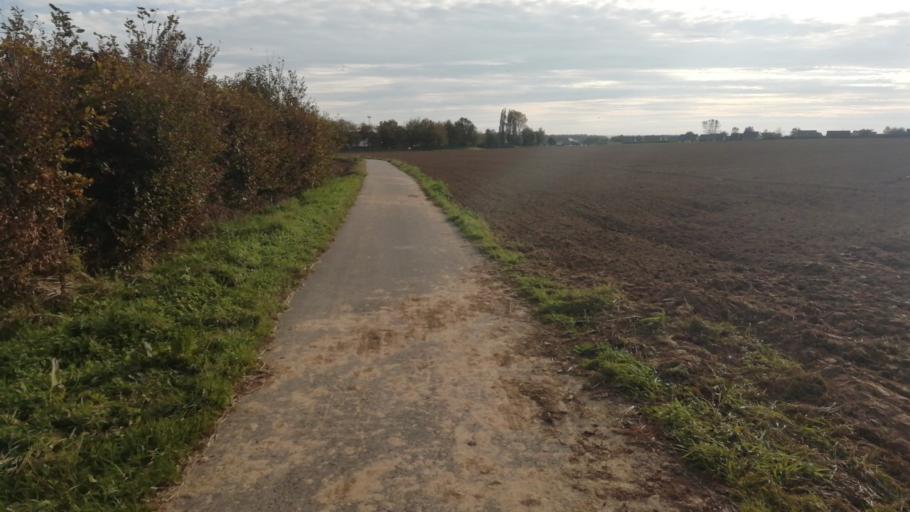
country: FR
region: Haute-Normandie
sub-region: Departement de la Seine-Maritime
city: Rogerville
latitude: 49.5099
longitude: 0.2639
